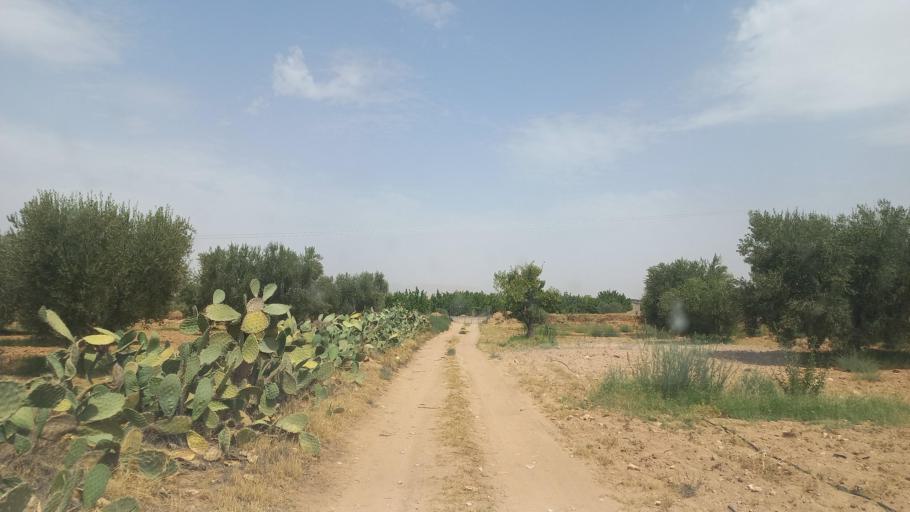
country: TN
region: Al Qasrayn
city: Kasserine
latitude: 35.2642
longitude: 9.0006
